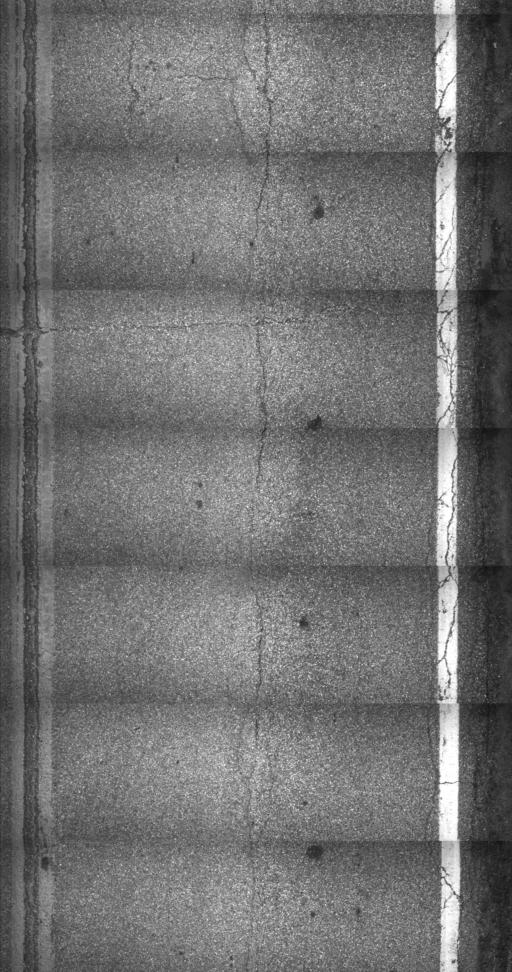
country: US
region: Vermont
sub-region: Rutland County
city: West Rutland
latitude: 43.6761
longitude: -73.0270
